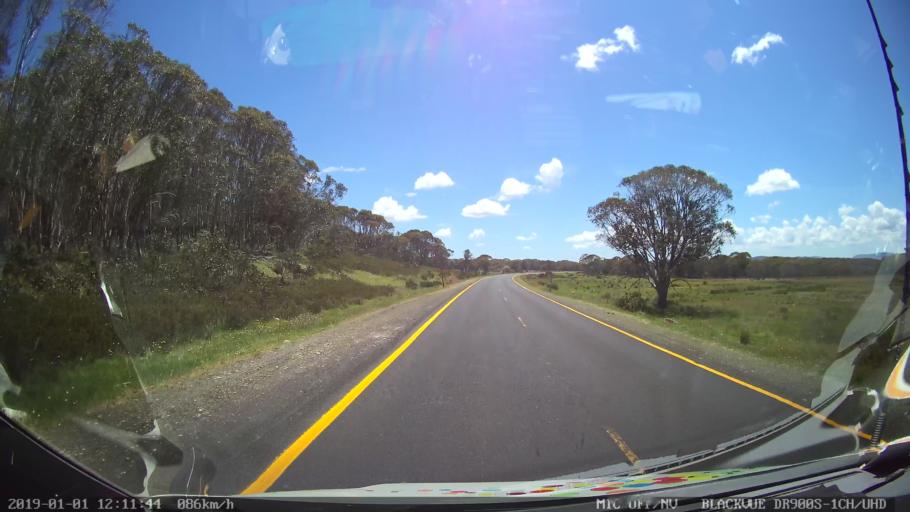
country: AU
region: New South Wales
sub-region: Tumut Shire
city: Tumut
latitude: -35.7805
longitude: 148.5089
